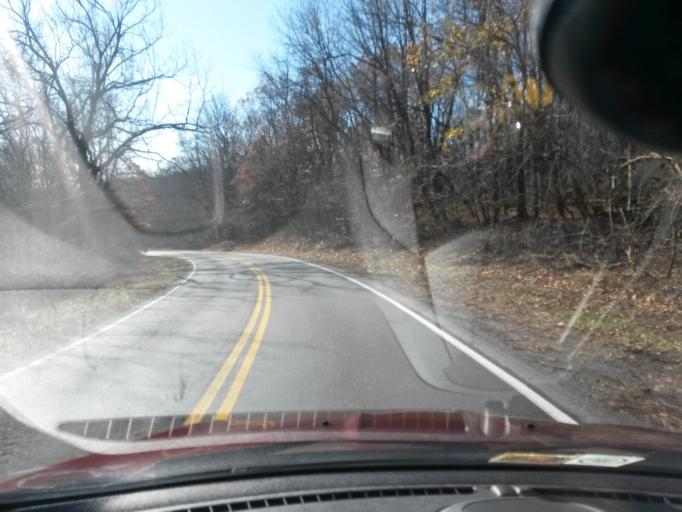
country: US
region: Virginia
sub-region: City of Bedford
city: Bedford
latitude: 37.4327
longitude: -79.5750
